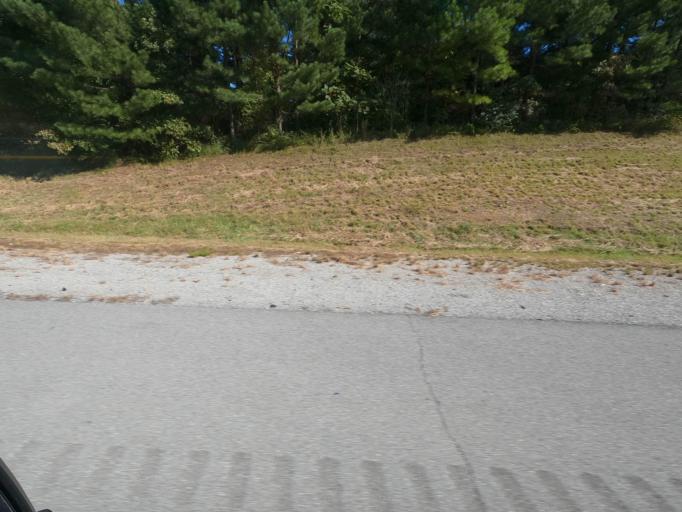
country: US
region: Tennessee
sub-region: Williamson County
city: Fairview
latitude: 35.9253
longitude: -87.1763
